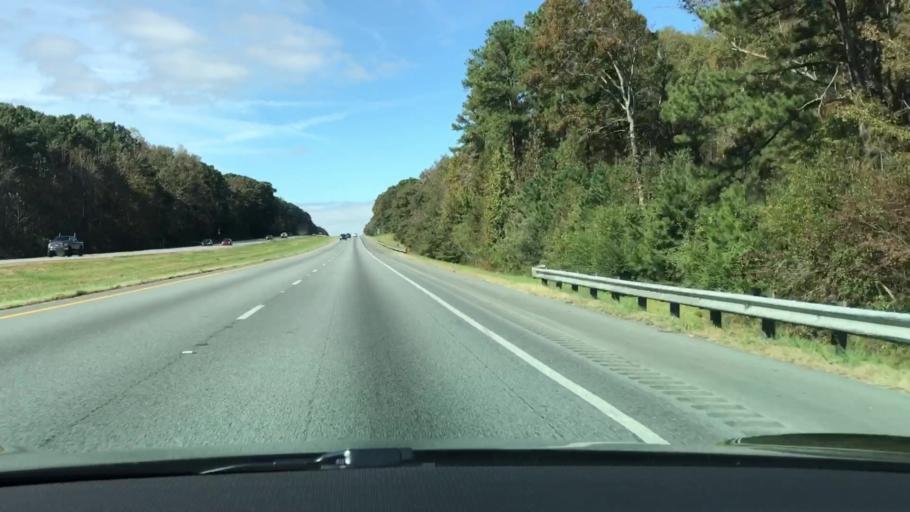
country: US
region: Georgia
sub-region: Morgan County
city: Madison
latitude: 33.5824
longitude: -83.5929
